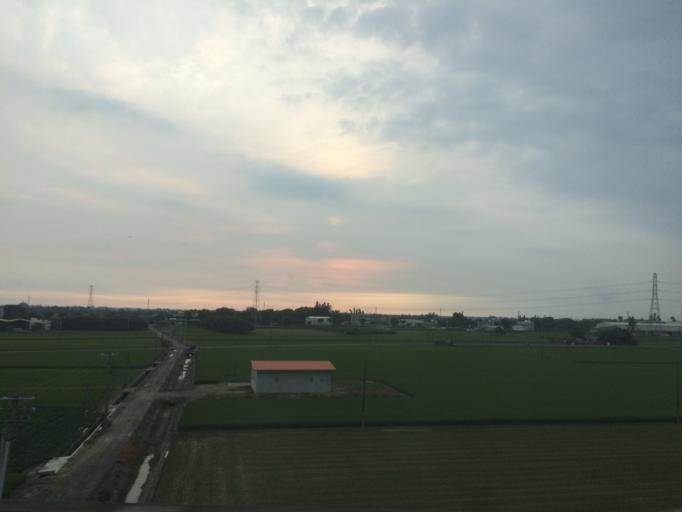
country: TW
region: Taiwan
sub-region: Chiayi
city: Taibao
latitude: 23.6219
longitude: 120.3394
